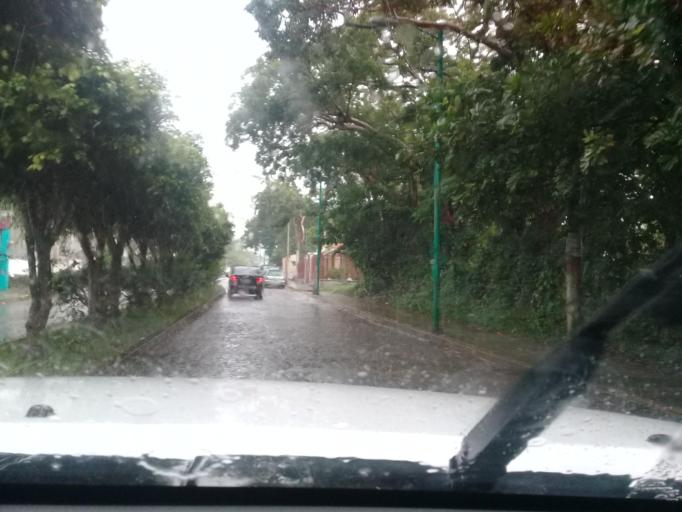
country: MX
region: Veracruz
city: Santiago Tuxtla
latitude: 18.4616
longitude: -95.3093
